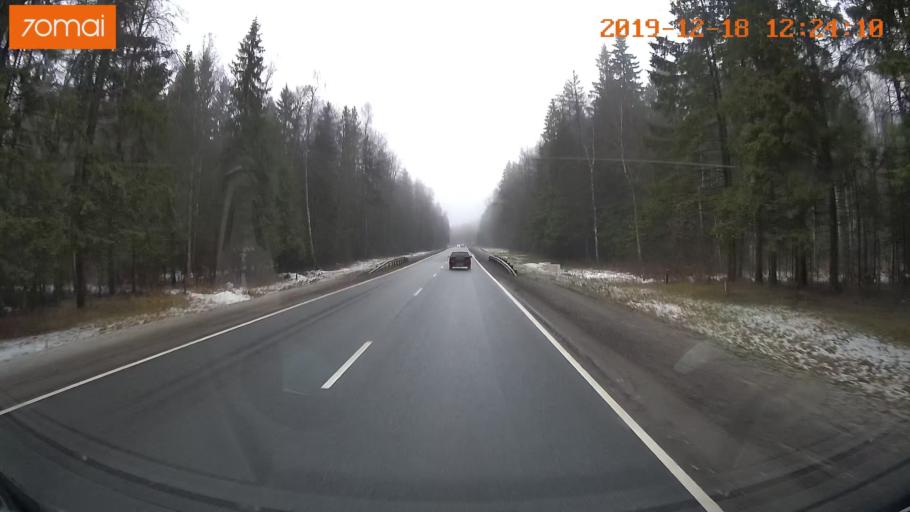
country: RU
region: Moskovskaya
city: Novopetrovskoye
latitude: 56.0212
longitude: 36.4996
